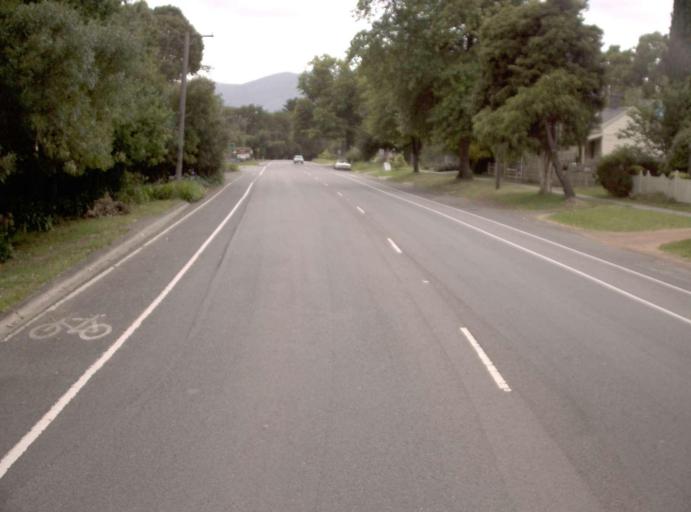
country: AU
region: Victoria
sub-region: Yarra Ranges
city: Healesville
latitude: -37.6569
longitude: 145.5111
